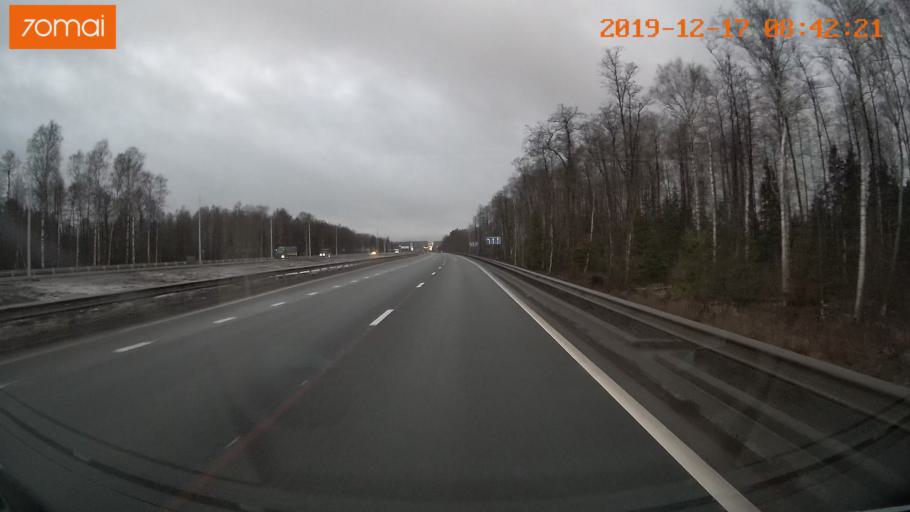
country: RU
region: Vladimir
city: Kosterevo
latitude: 55.9639
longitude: 39.7445
